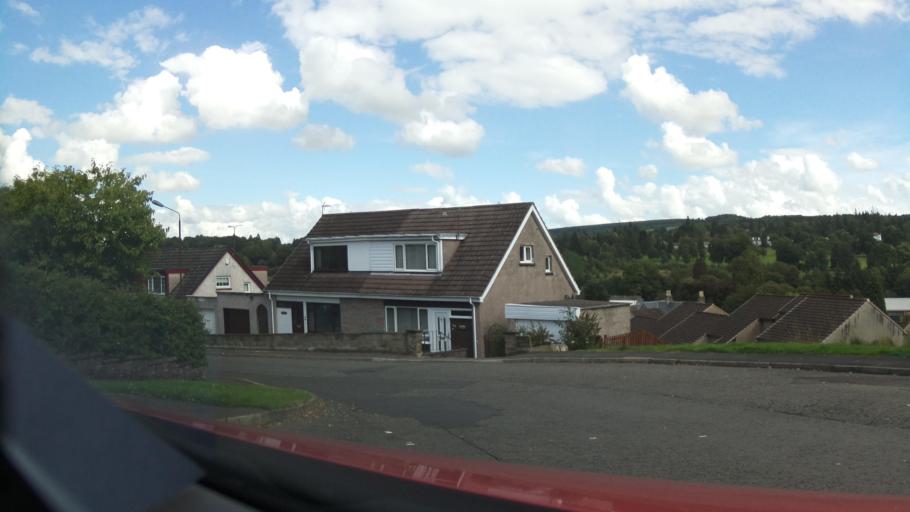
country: GB
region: Scotland
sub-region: Stirling
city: Dunblane
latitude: 56.1823
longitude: -3.9689
